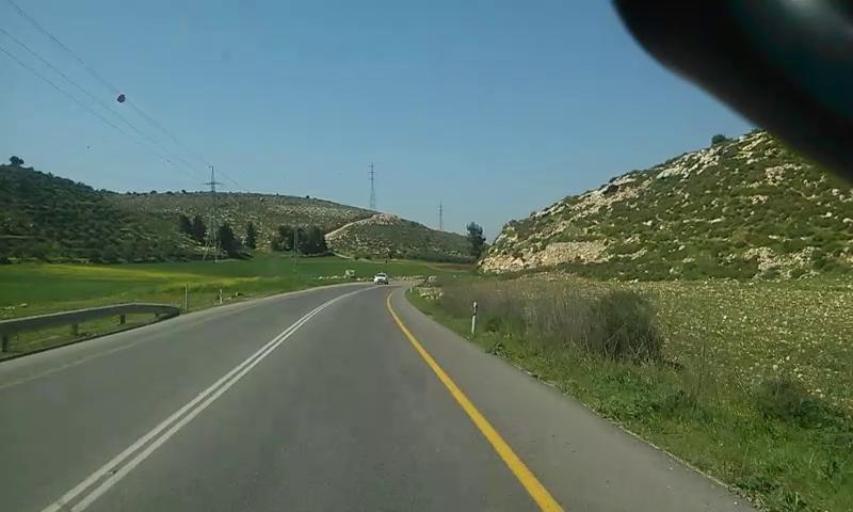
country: PS
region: West Bank
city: Idhna
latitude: 31.5822
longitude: 34.9742
